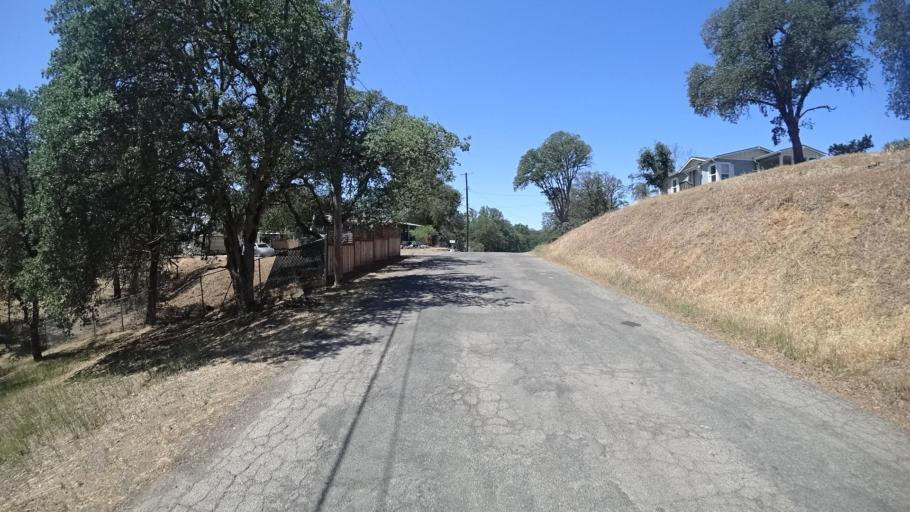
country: US
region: California
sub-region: Lake County
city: Lower Lake
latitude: 38.9144
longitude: -122.5958
